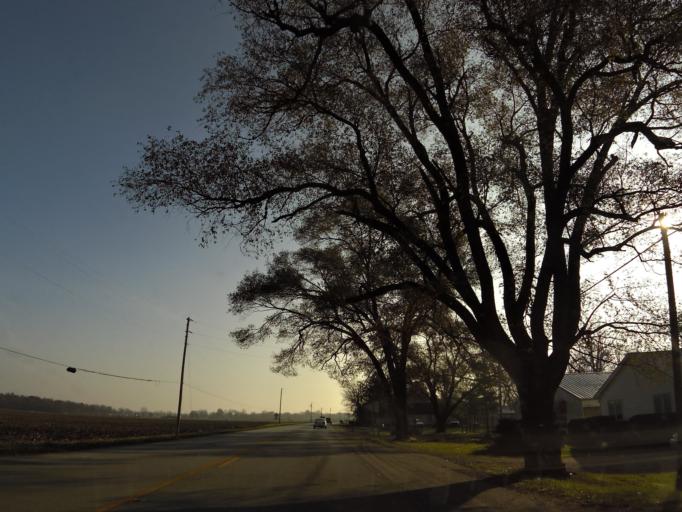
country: US
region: Indiana
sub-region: Hendricks County
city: Fairfield Heights
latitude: 39.8310
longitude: -86.3615
